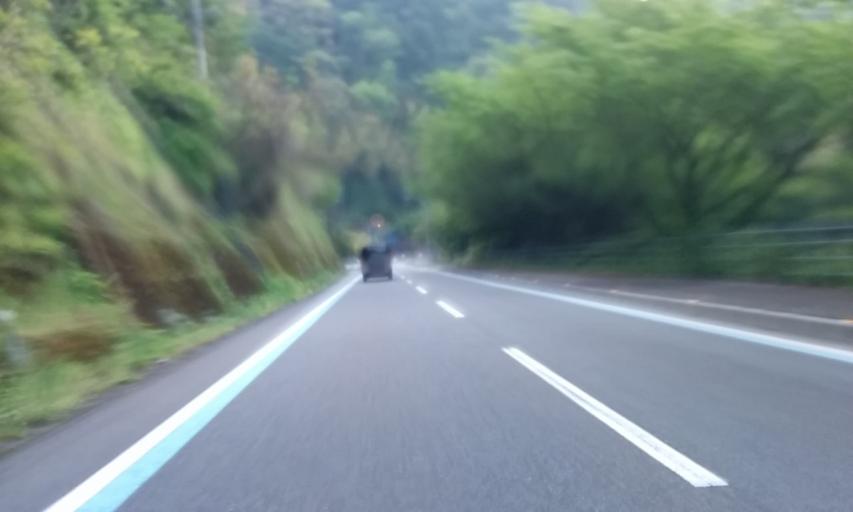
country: JP
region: Ehime
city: Saijo
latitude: 33.8498
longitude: 133.2029
